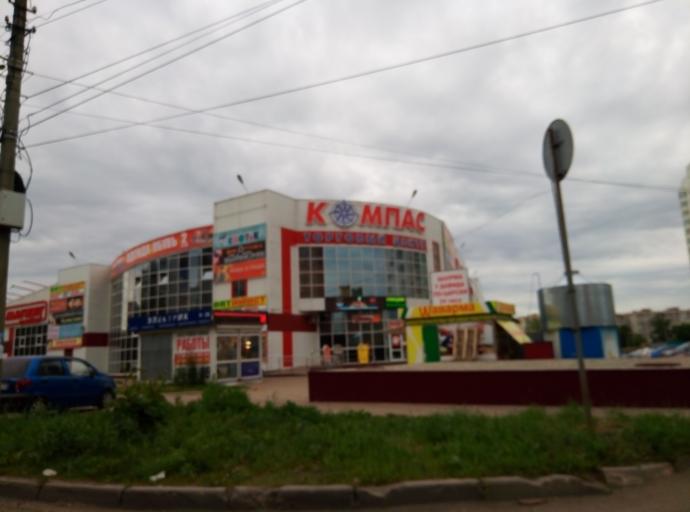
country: RU
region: Kursk
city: Kursk
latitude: 51.7272
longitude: 36.1407
